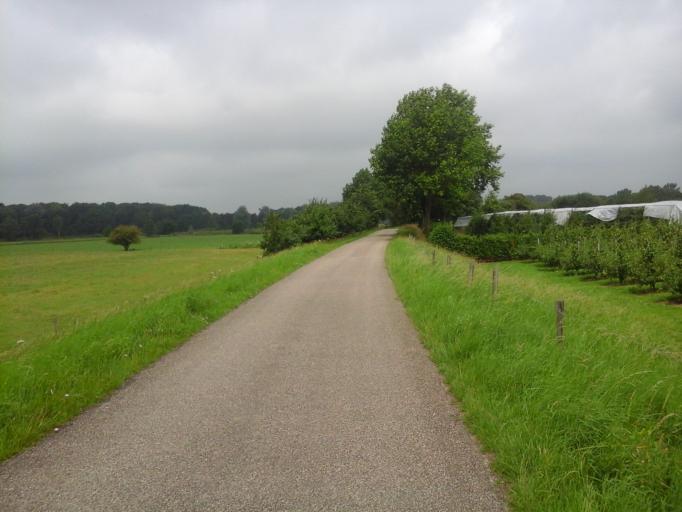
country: NL
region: Gelderland
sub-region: Gemeente Geldermalsen
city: Geldermalsen
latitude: 51.8904
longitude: 5.2493
